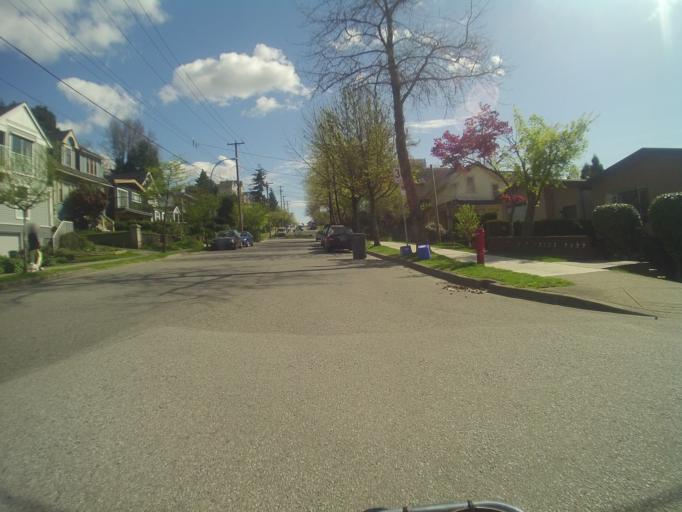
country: CA
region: British Columbia
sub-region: Fraser Valley Regional District
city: North Vancouver
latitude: 49.2720
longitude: -123.0735
